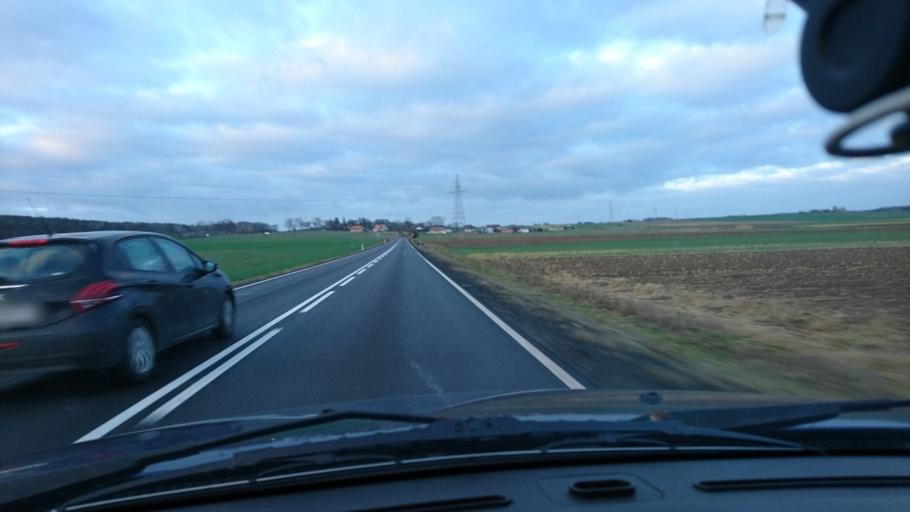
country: PL
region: Greater Poland Voivodeship
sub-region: Powiat ostrzeszowski
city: Ostrzeszow
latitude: 51.3614
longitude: 17.9463
